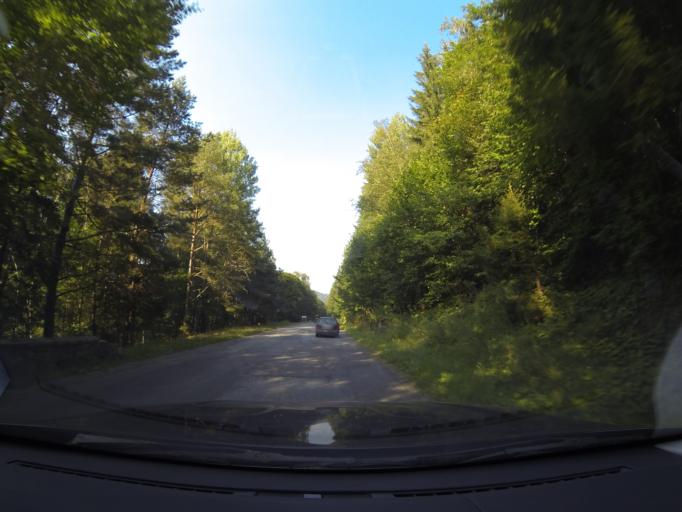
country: RO
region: Arges
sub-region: Comuna Arefu
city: Arefu
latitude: 45.3960
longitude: 24.6353
